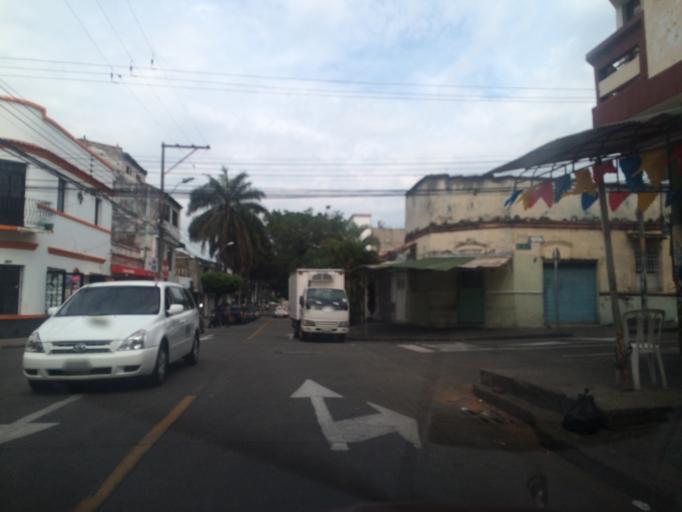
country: CO
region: Valle del Cauca
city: Cali
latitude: 3.4413
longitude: -76.5395
